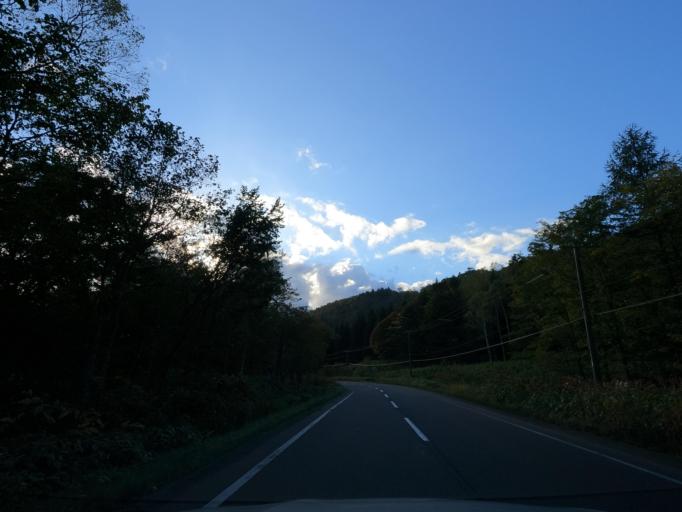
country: JP
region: Hokkaido
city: Shiraoi
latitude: 42.7045
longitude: 141.1426
